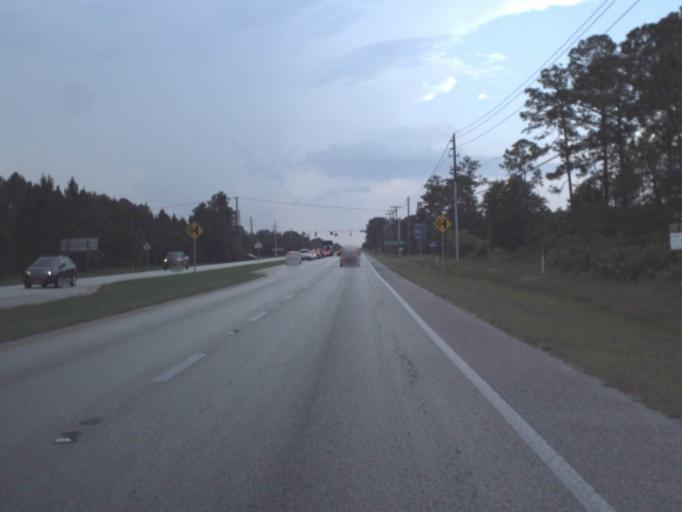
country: US
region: Florida
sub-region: Saint Johns County
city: Palm Valley
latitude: 30.0789
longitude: -81.4527
